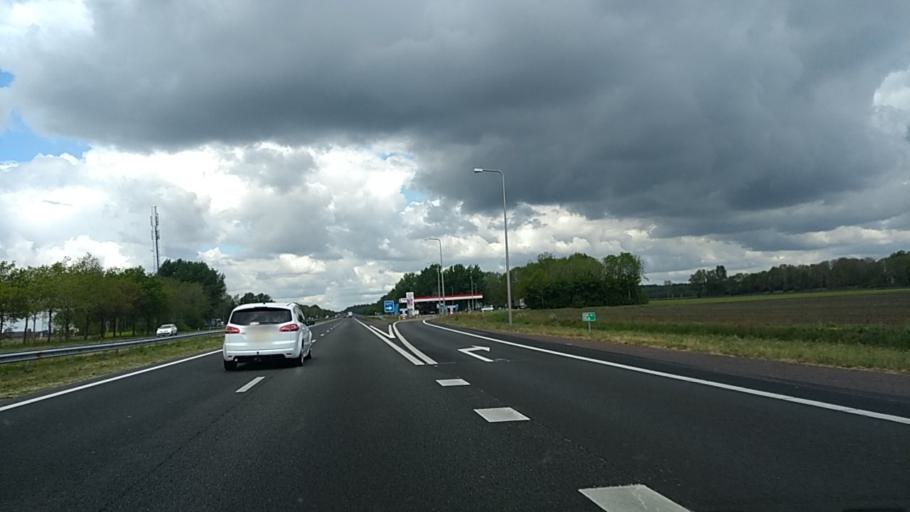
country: NL
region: Drenthe
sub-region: Gemeente Meppel
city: Meppel
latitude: 52.7492
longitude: 6.1902
